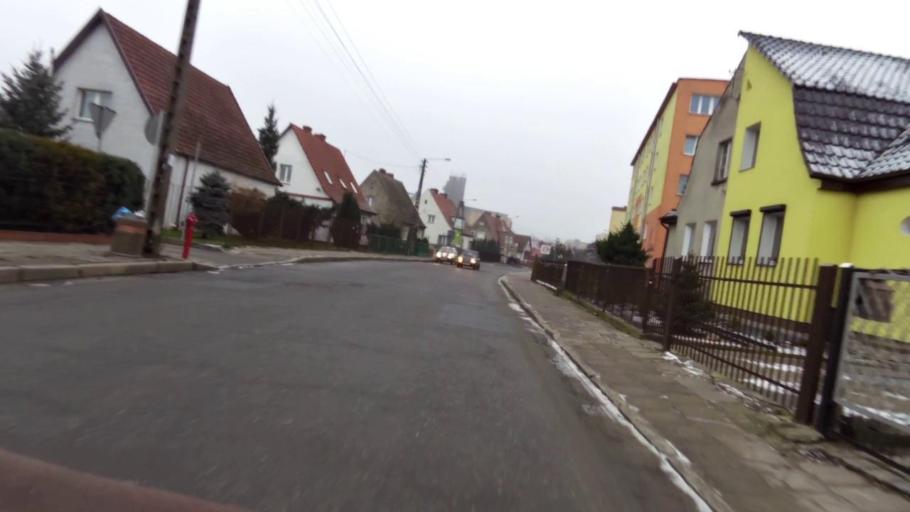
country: PL
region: West Pomeranian Voivodeship
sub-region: Powiat walecki
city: Walcz
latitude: 53.2793
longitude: 16.4770
